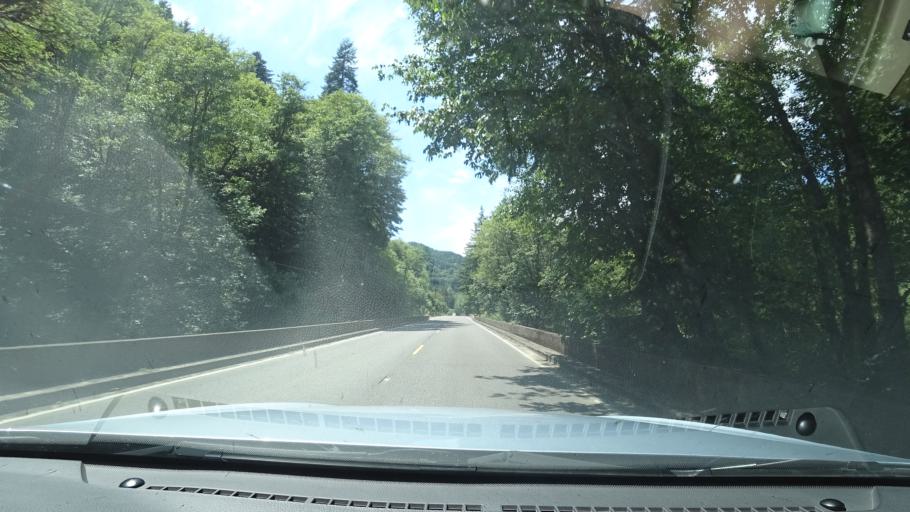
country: US
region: Oregon
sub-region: Lane County
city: Florence
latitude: 44.0271
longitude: -123.8297
